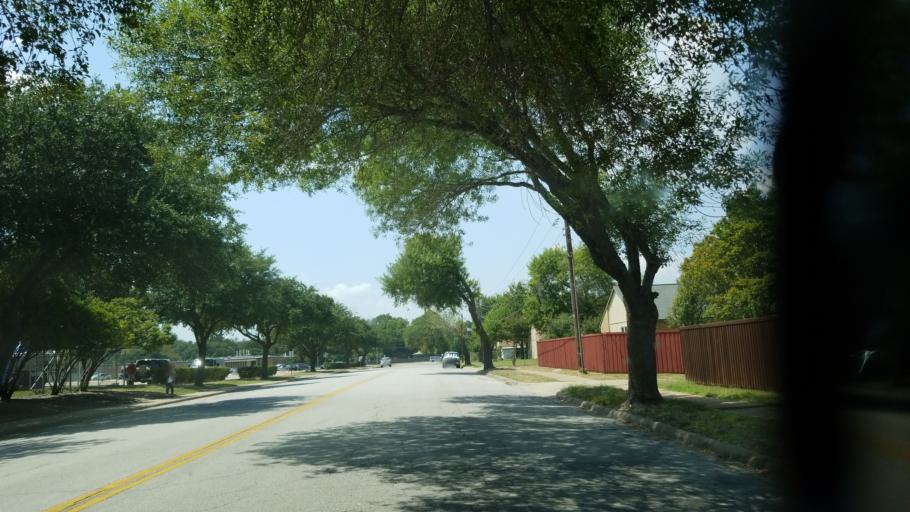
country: US
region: Texas
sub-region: Dallas County
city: Garland
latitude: 32.9266
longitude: -96.6364
